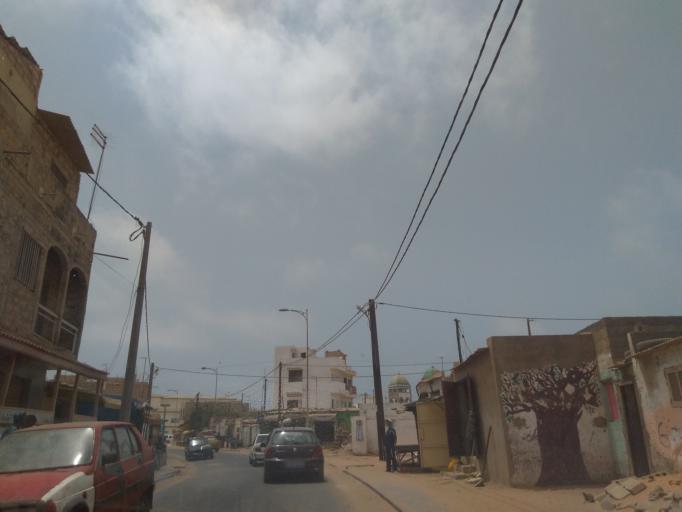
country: SN
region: Dakar
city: Pikine
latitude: 14.7685
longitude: -17.4297
